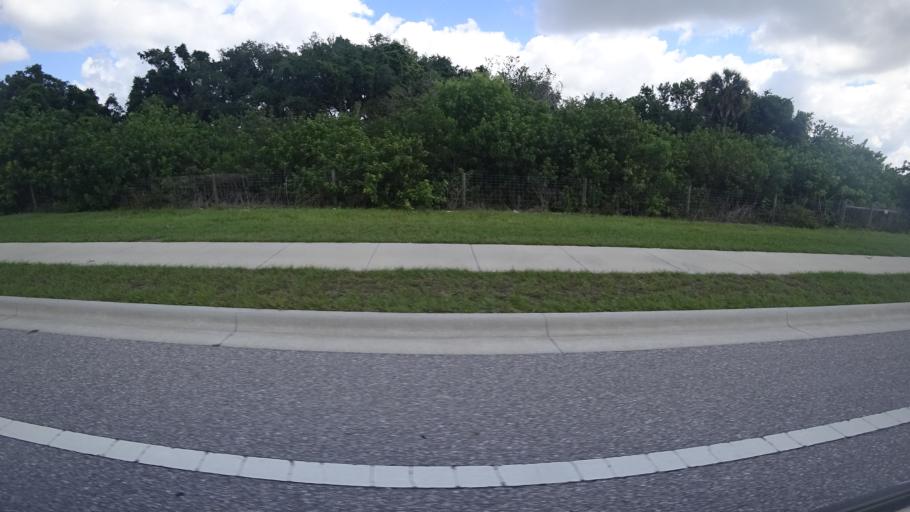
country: US
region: Florida
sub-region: Manatee County
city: Longboat Key
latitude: 27.4419
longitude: -82.6332
